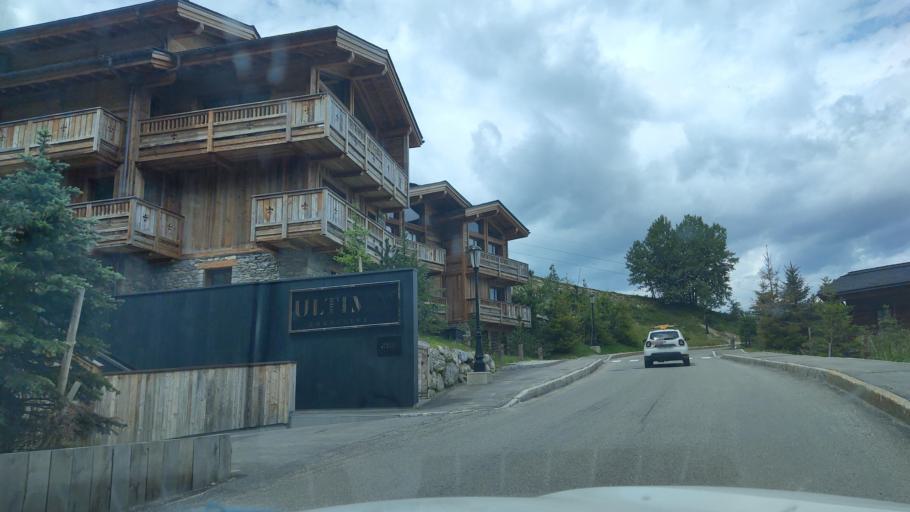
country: FR
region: Rhone-Alpes
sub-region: Departement de la Savoie
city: Courchevel
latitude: 45.4139
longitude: 6.6565
